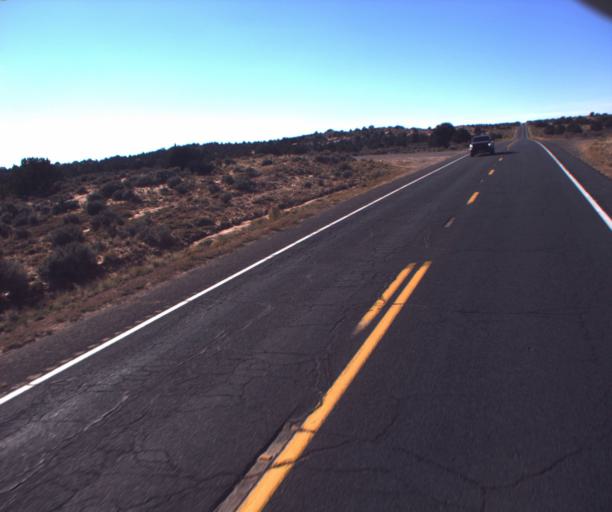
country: US
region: Arizona
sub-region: Coconino County
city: Kaibito
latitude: 36.5781
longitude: -110.7808
